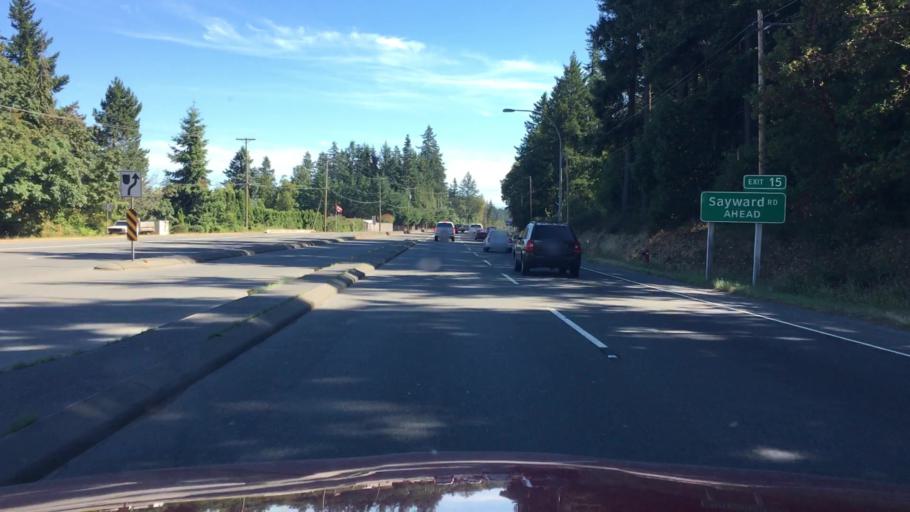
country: CA
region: British Columbia
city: Victoria
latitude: 48.5442
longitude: -123.3907
